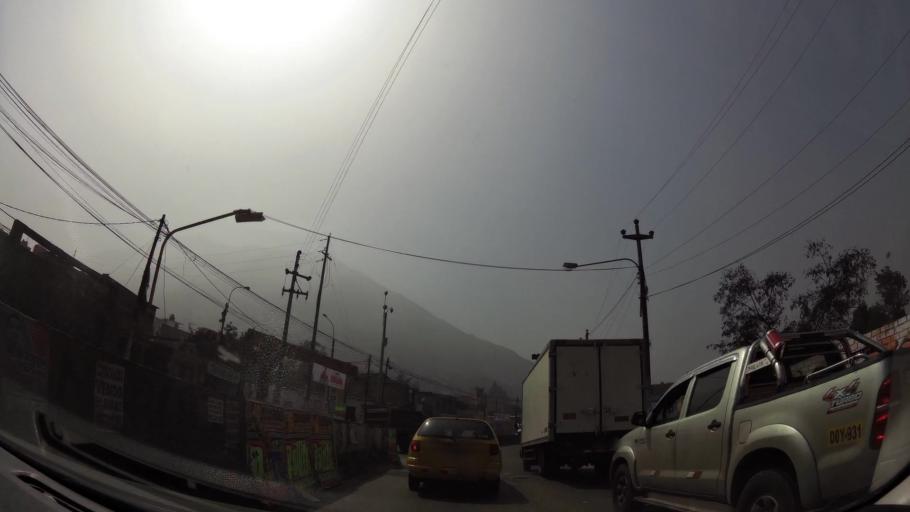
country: PE
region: Lima
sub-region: Lima
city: Chosica
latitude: -11.9444
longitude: -76.7095
